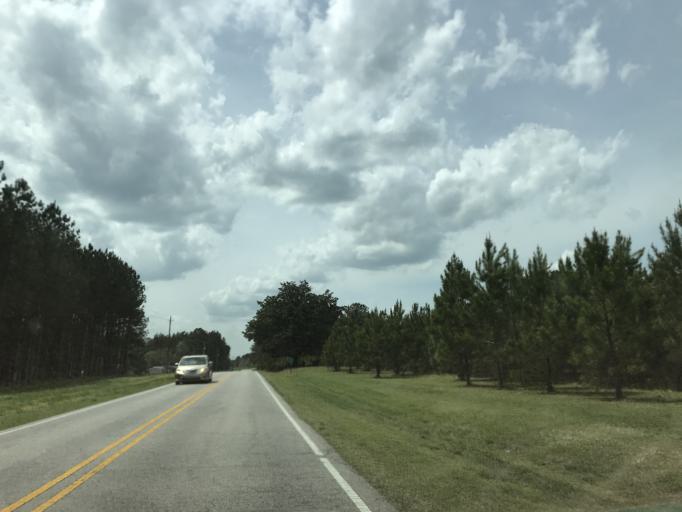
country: US
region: North Carolina
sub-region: Nash County
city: Spring Hope
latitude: 35.9660
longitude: -78.2272
